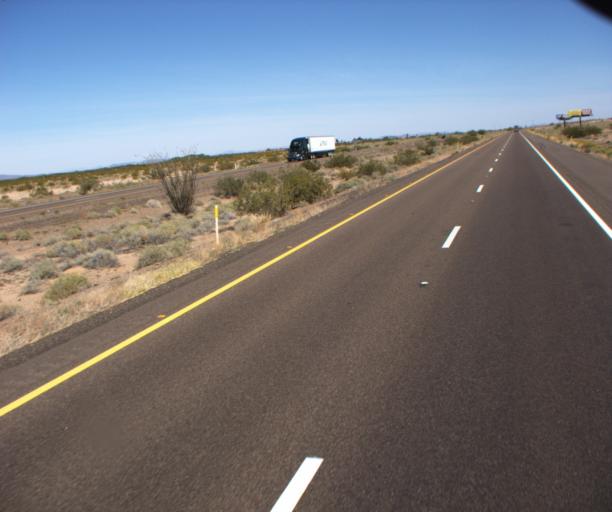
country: US
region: Arizona
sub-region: Yuma County
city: Wellton
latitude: 32.7941
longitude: -113.5524
